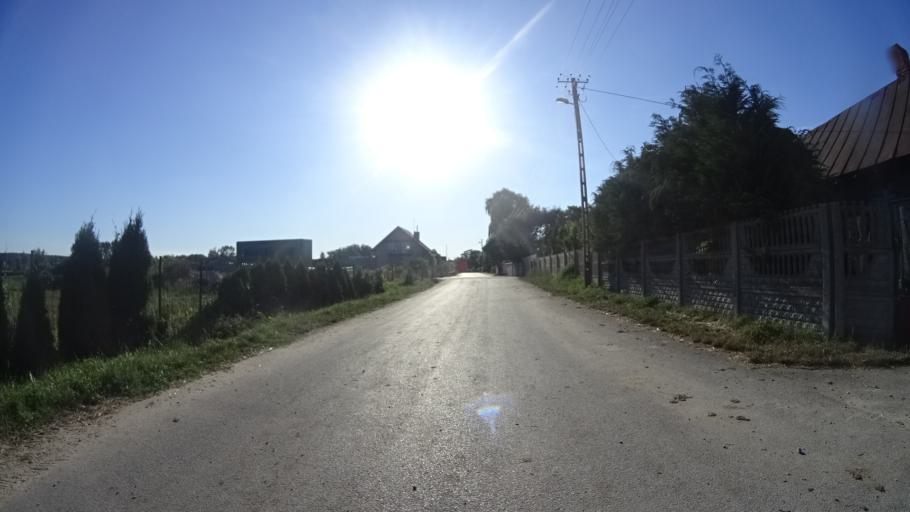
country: PL
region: Masovian Voivodeship
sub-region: Powiat bialobrzeski
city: Wysmierzyce
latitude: 51.6568
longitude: 20.7855
